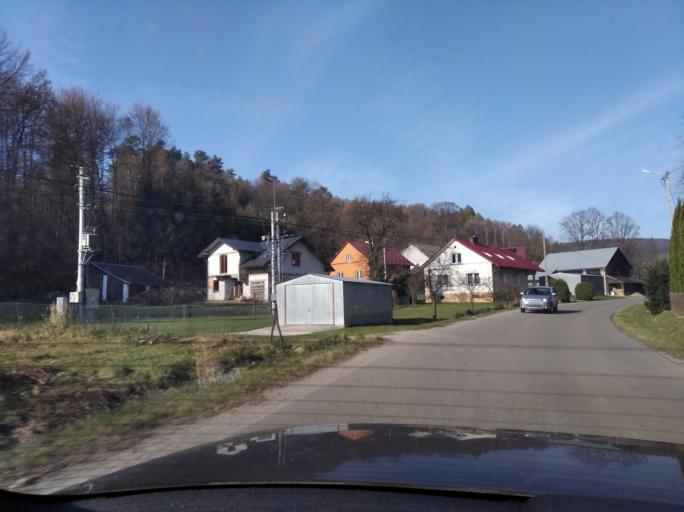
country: PL
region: Subcarpathian Voivodeship
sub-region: Powiat strzyzowski
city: Frysztak
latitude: 49.8883
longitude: 21.6028
